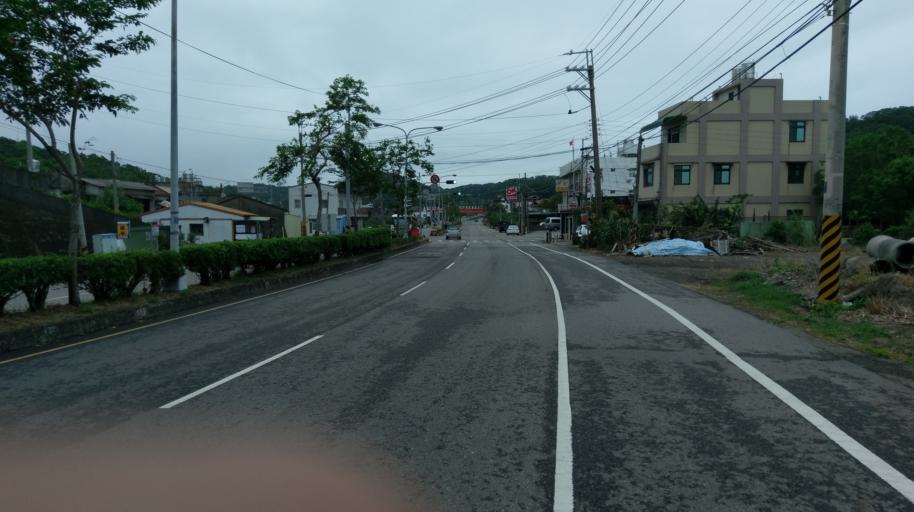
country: TW
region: Taiwan
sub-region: Miaoli
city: Miaoli
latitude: 24.6543
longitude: 120.8538
